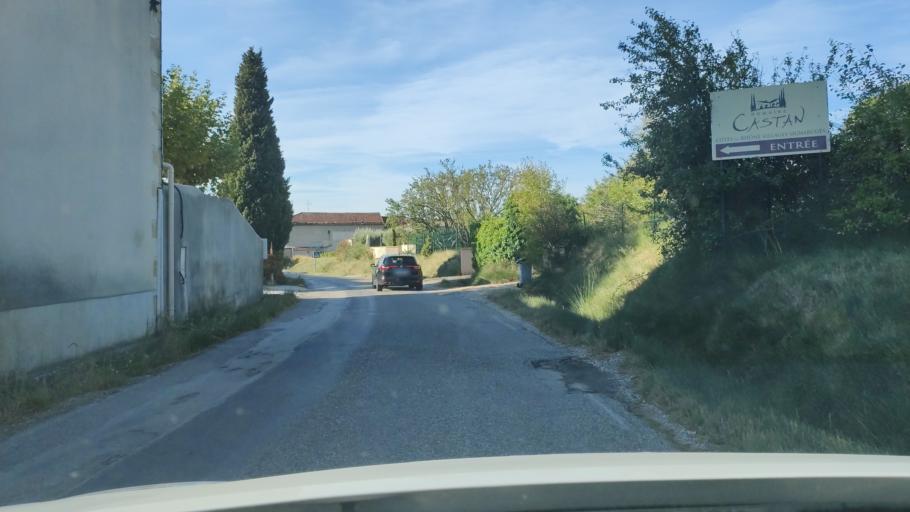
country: FR
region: Languedoc-Roussillon
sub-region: Departement du Gard
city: Saze
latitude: 43.9330
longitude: 4.6512
